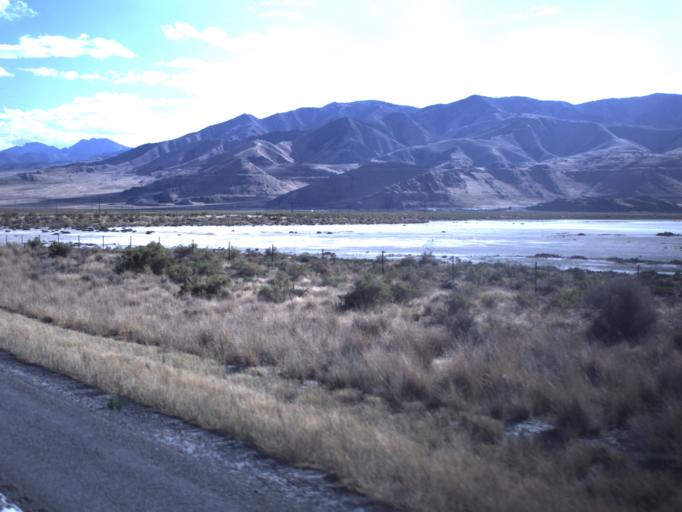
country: US
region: Utah
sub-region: Tooele County
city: Grantsville
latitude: 40.7014
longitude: -112.5299
